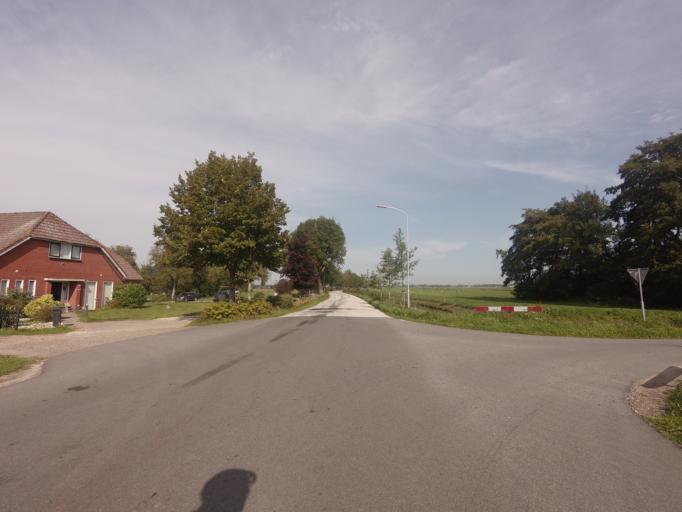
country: NL
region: Groningen
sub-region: Gemeente Leek
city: Leek
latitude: 53.2019
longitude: 6.3499
